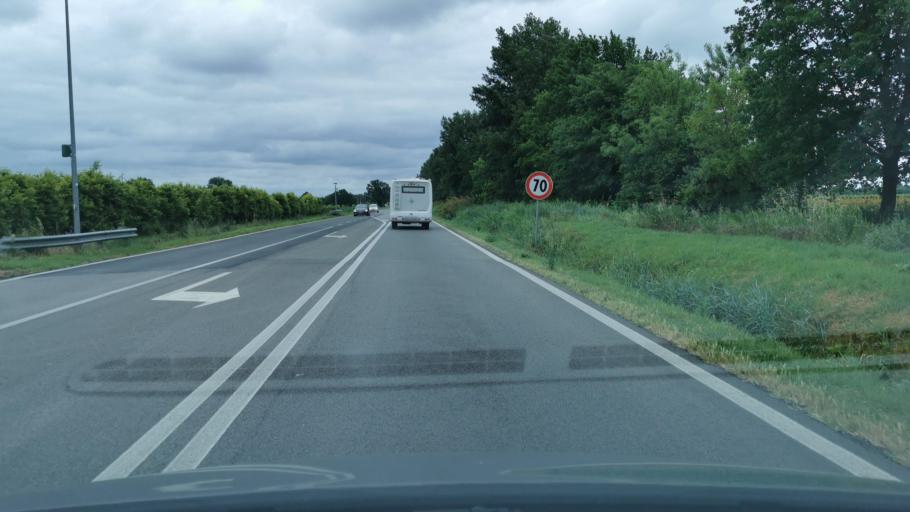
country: IT
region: Emilia-Romagna
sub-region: Provincia di Ravenna
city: Granarolo
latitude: 44.3438
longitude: 11.9223
